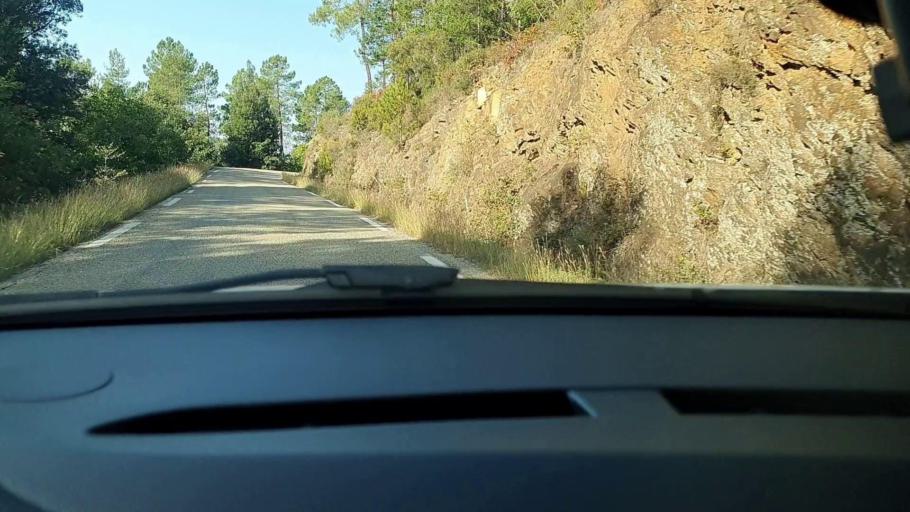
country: FR
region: Languedoc-Roussillon
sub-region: Departement du Gard
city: Besseges
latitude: 44.3235
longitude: 4.0745
